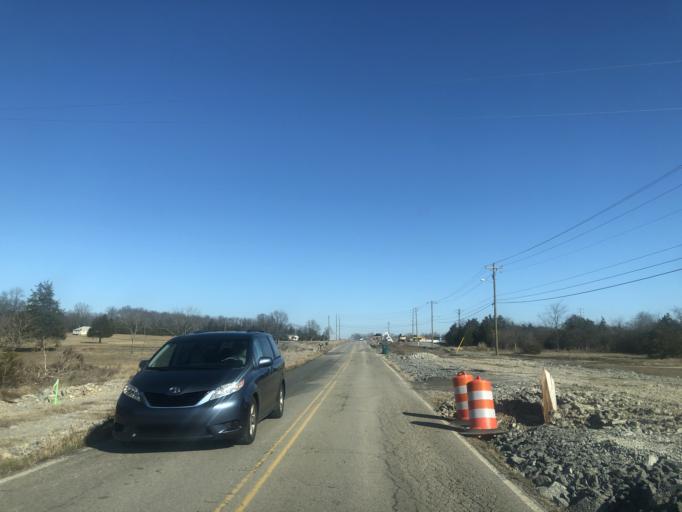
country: US
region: Tennessee
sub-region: Rutherford County
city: Smyrna
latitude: 35.9582
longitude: -86.5438
